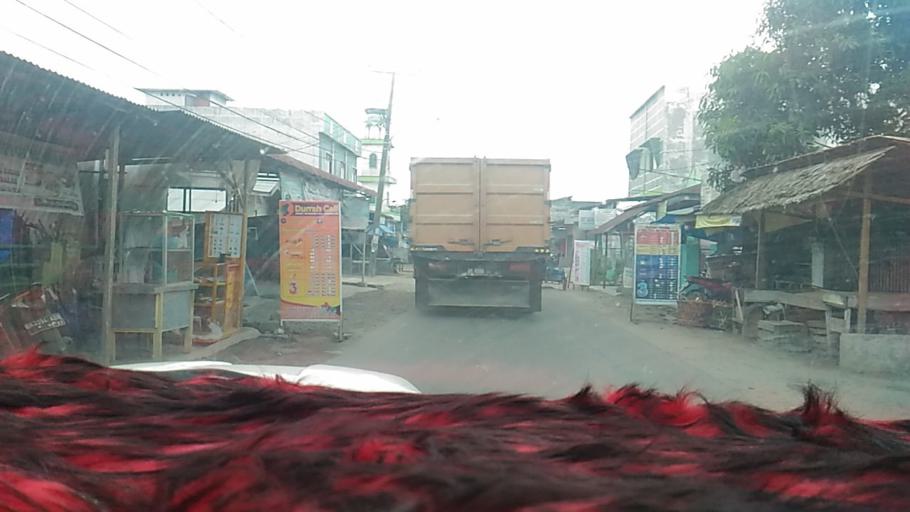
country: ID
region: North Sumatra
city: Binjai
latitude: 3.5978
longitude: 98.5516
